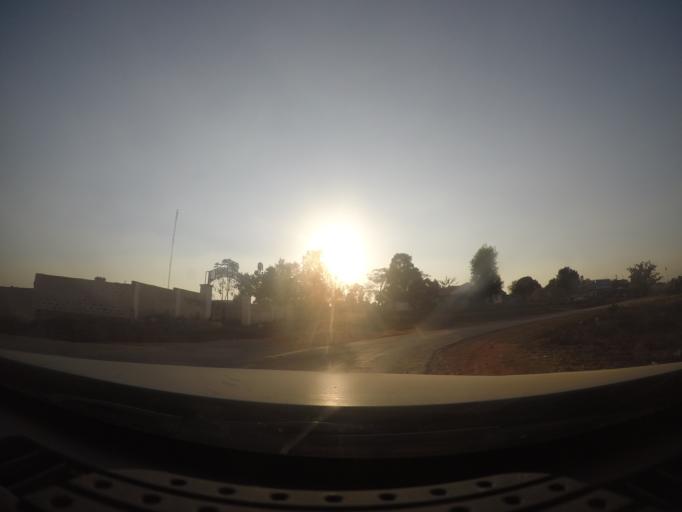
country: MM
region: Shan
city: Taunggyi
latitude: 20.4490
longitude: 97.1342
